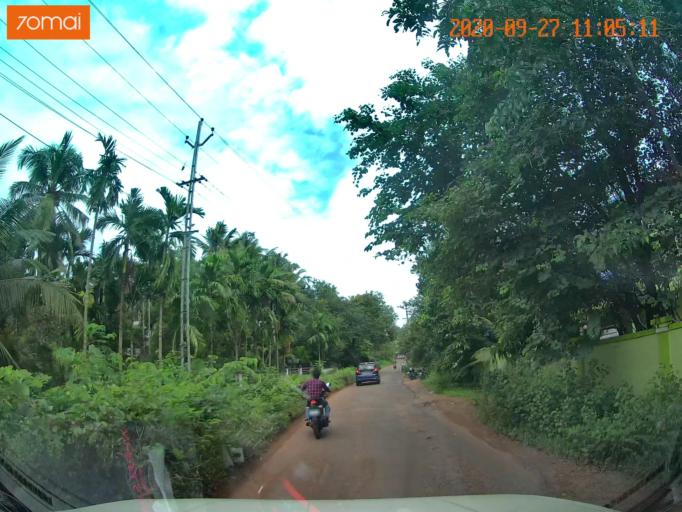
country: IN
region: Kerala
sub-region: Thrissur District
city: Irinjalakuda
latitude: 10.4228
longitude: 76.2488
